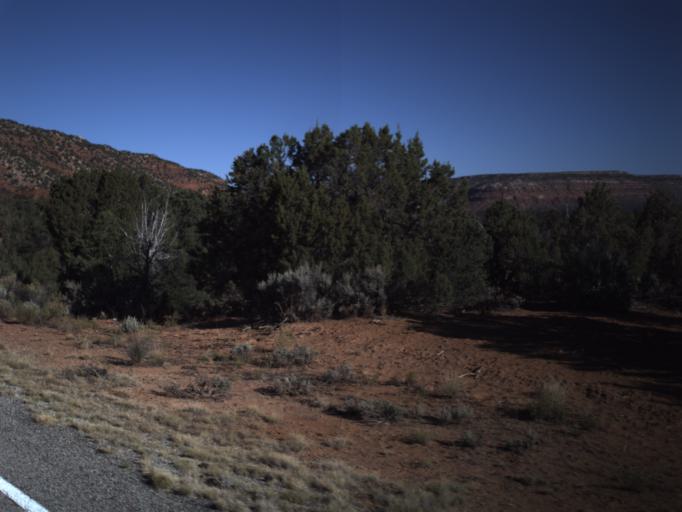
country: US
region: Utah
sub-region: San Juan County
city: Blanding
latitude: 37.5677
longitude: -110.0333
